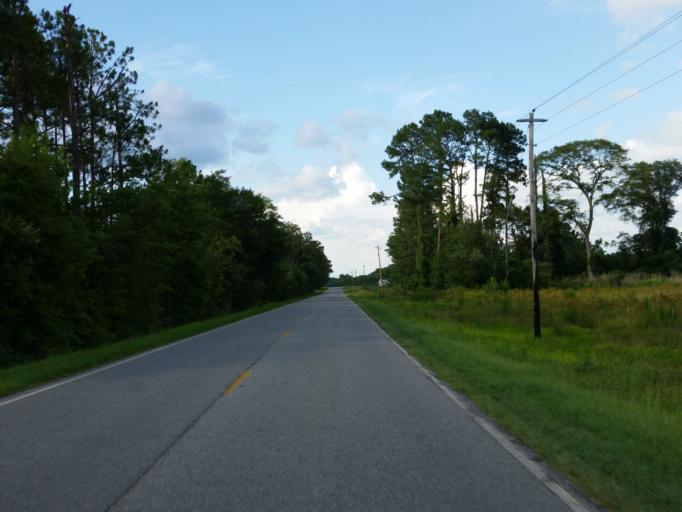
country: US
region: Georgia
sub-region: Crisp County
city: Cordele
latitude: 32.0183
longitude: -83.8474
